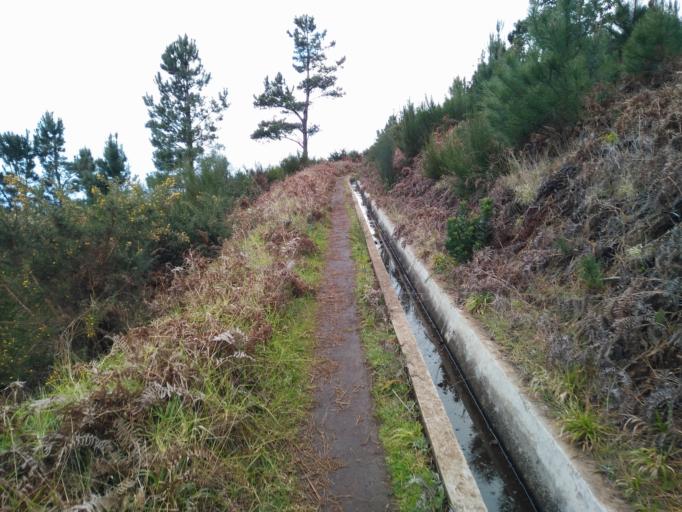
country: PT
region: Madeira
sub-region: Calheta
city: Faja da Ovelha
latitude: 32.8175
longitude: -17.2292
